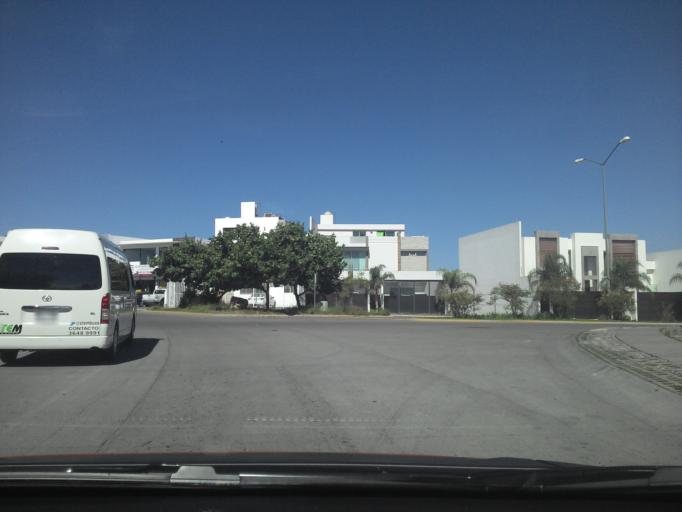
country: MX
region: Jalisco
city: Nuevo Mexico
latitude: 20.7478
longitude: -103.4112
